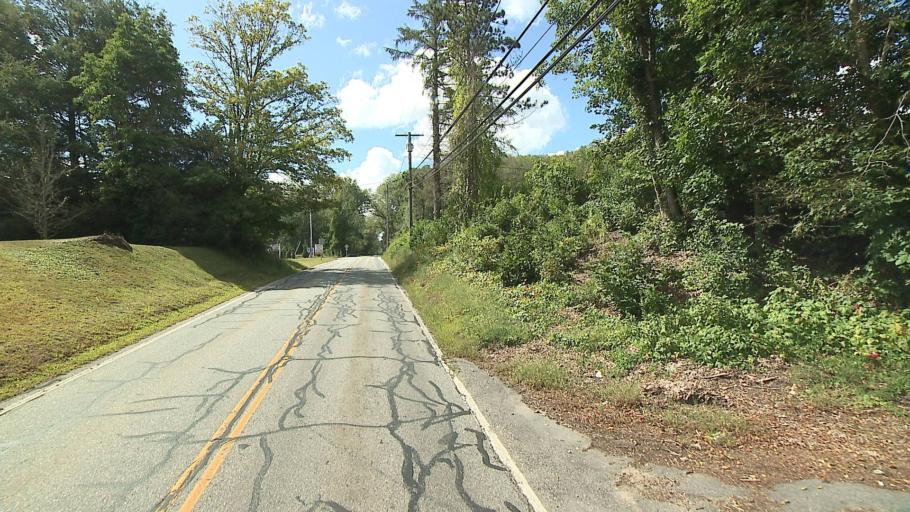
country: US
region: Connecticut
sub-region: Windham County
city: Putnam
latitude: 41.9067
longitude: -71.9196
